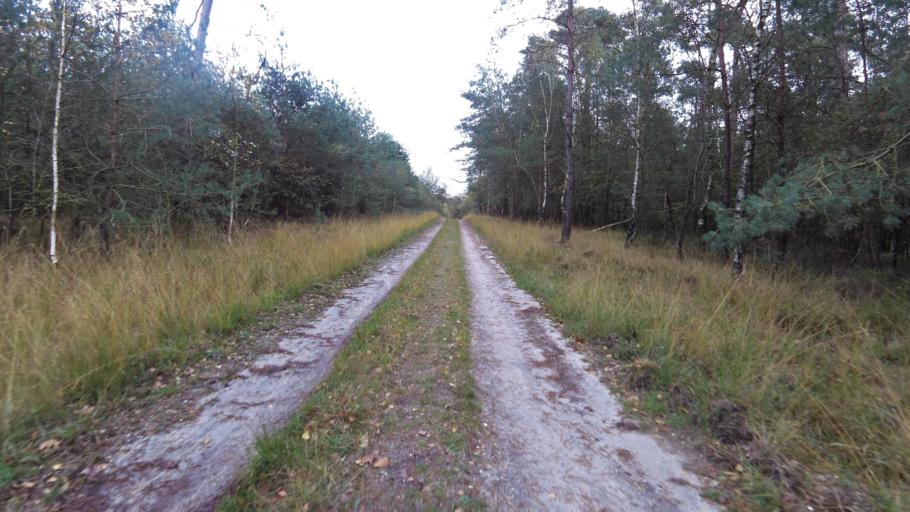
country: NL
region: Gelderland
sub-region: Gemeente Apeldoorn
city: Uddel
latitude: 52.3070
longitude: 5.8470
